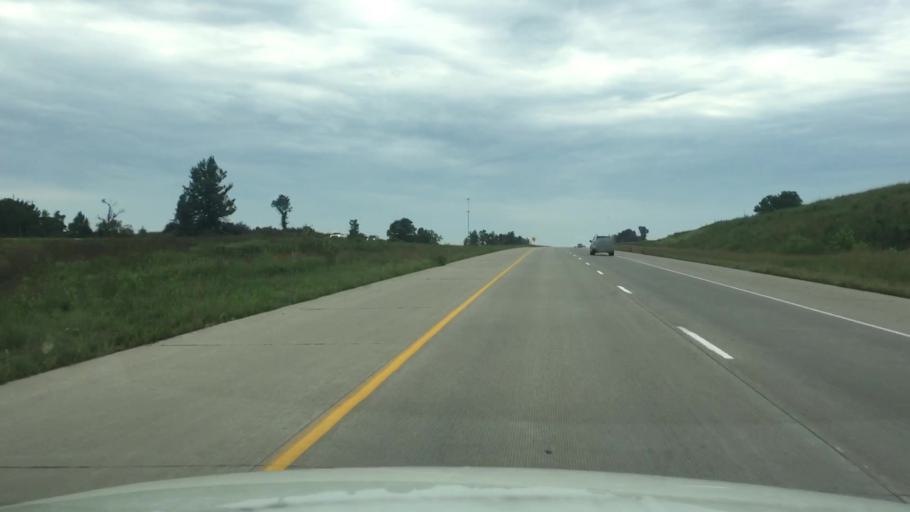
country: US
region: Iowa
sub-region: Warren County
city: Norwalk
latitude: 41.4521
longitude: -93.7801
